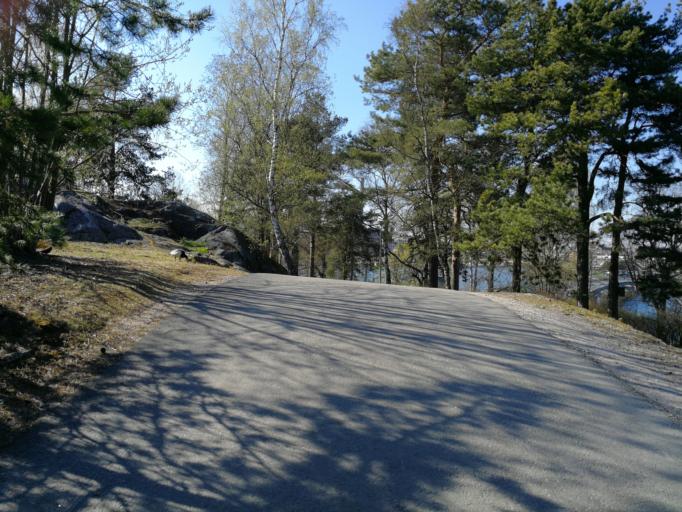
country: FI
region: Uusimaa
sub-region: Helsinki
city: Helsinki
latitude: 60.1763
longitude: 24.9843
